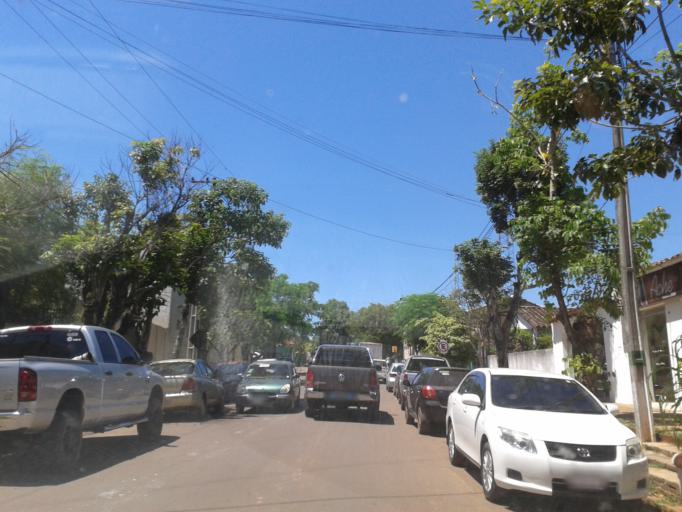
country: PY
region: Misiones
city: Santa Maria
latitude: -26.8863
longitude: -57.0257
